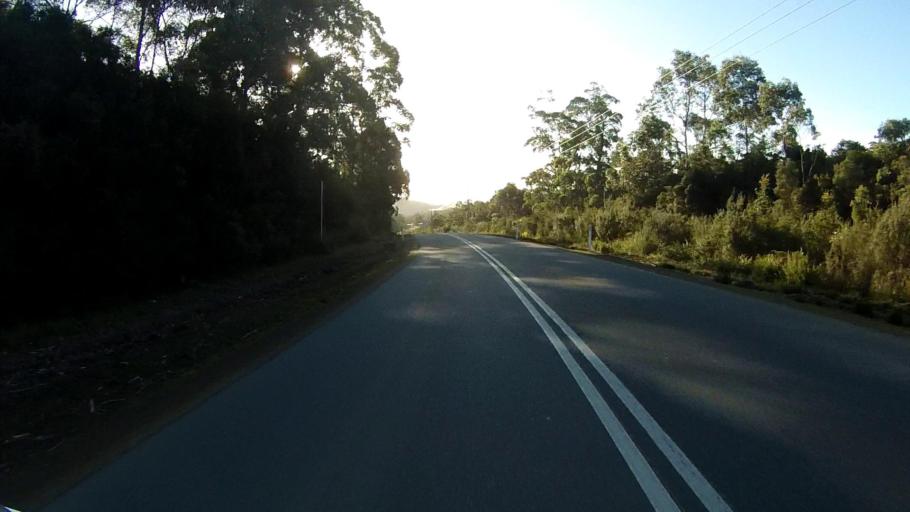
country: AU
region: Tasmania
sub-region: Clarence
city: Sandford
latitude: -43.0904
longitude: 147.8702
